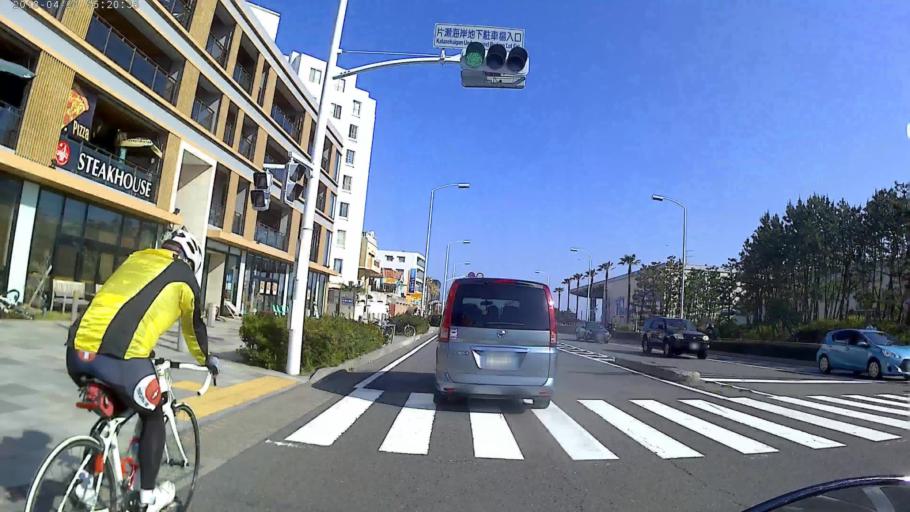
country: JP
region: Kanagawa
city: Fujisawa
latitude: 35.3107
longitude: 139.4795
